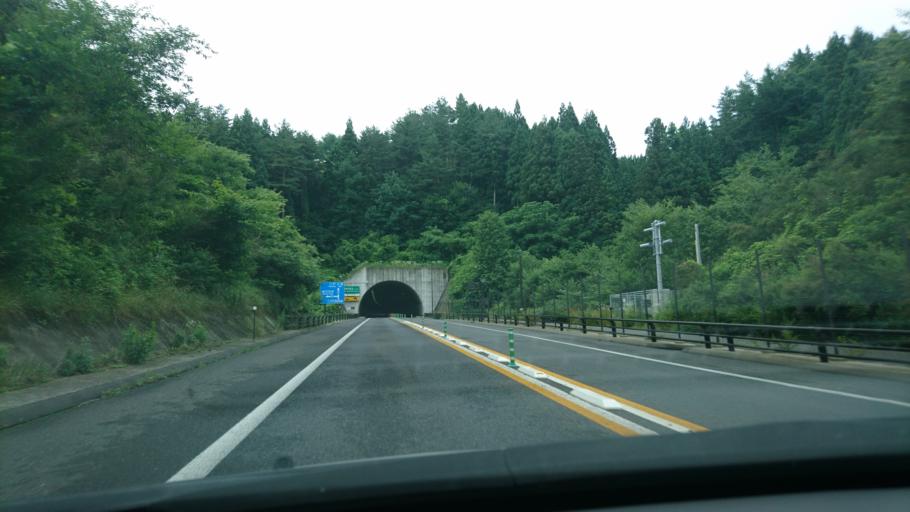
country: JP
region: Iwate
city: Miyako
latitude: 40.0156
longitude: 141.8851
